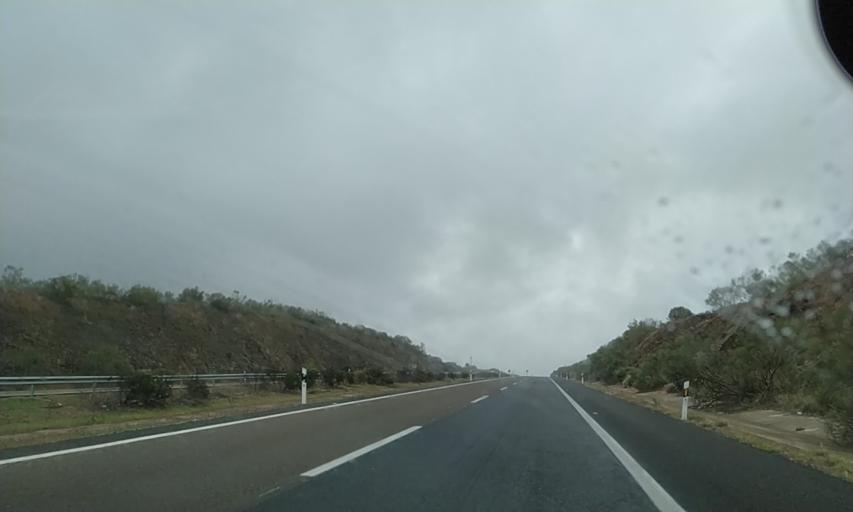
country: ES
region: Extremadura
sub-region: Provincia de Caceres
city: Casas de Millan
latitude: 39.8521
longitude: -6.3309
